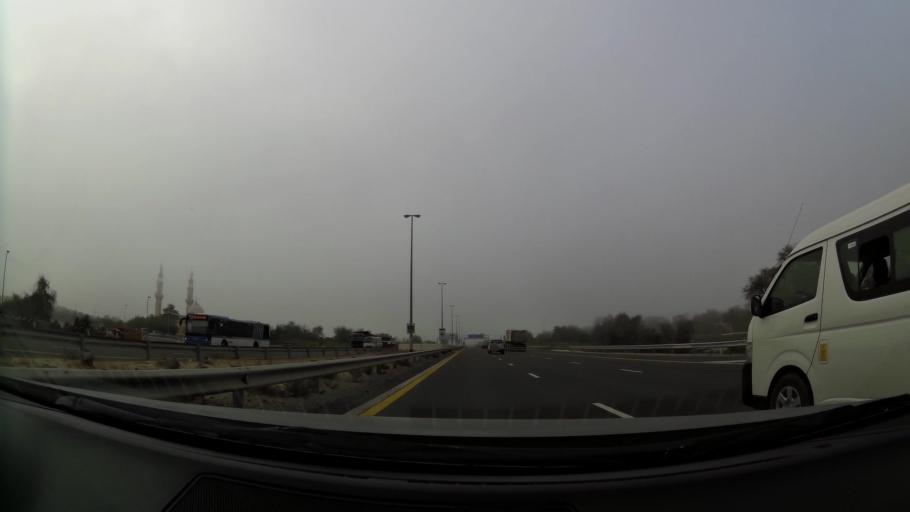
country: AE
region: Dubai
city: Dubai
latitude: 25.1607
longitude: 55.3317
